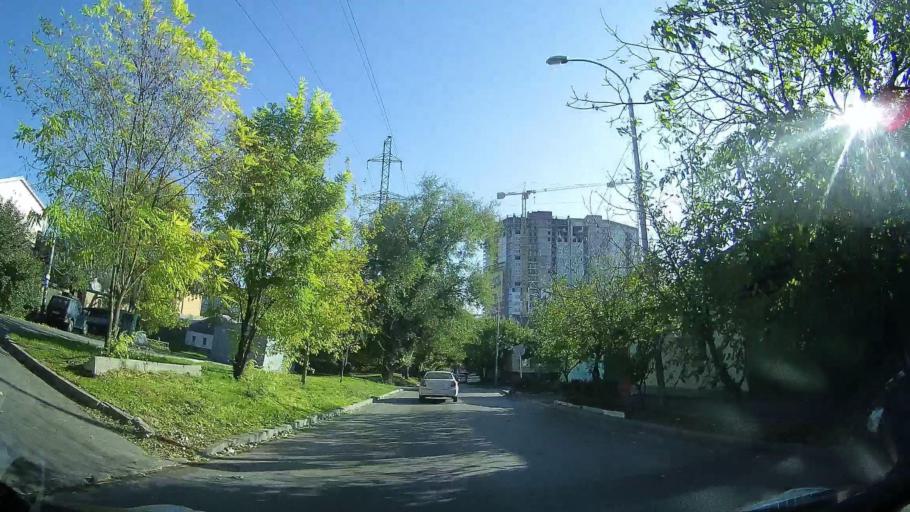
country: RU
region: Rostov
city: Rostov-na-Donu
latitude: 47.2281
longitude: 39.6908
